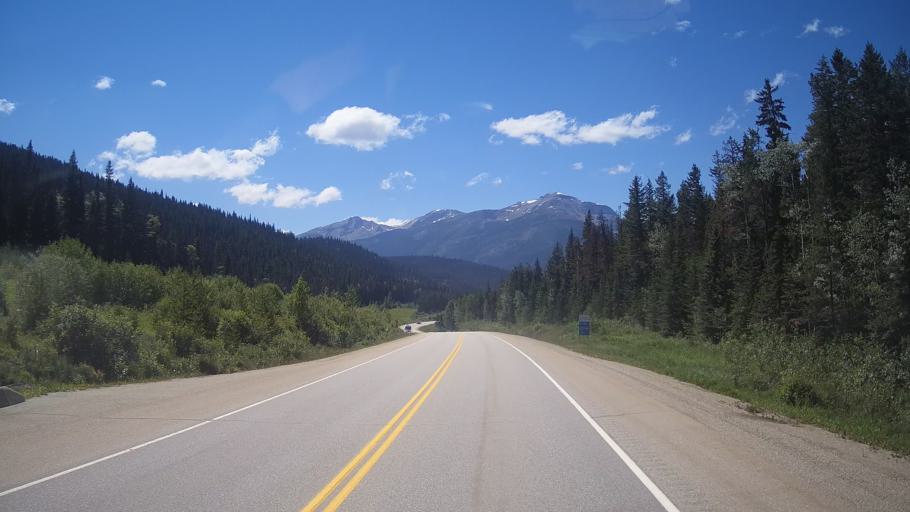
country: CA
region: Alberta
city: Jasper Park Lodge
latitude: 52.8624
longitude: -118.5298
